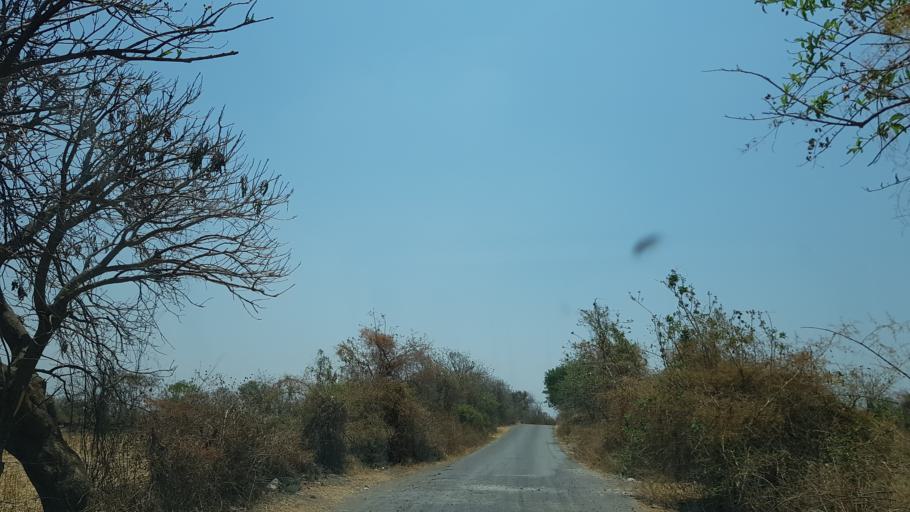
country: MX
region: Puebla
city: Huaquechula
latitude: 18.7867
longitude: -98.5448
